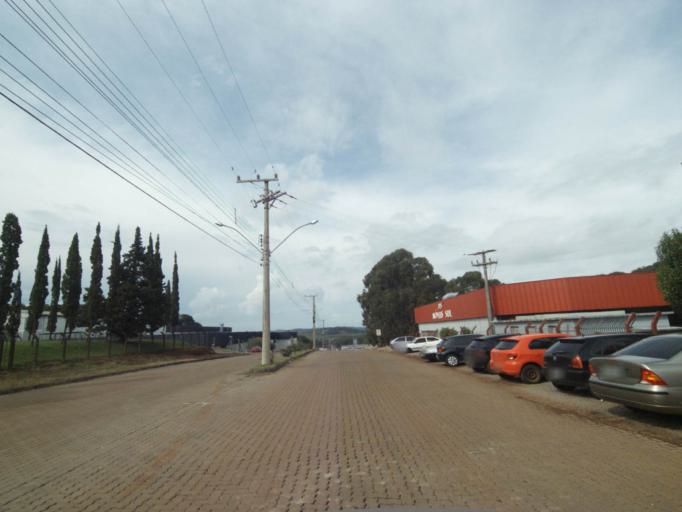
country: BR
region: Rio Grande do Sul
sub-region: Lagoa Vermelha
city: Lagoa Vermelha
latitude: -28.2265
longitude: -51.5110
